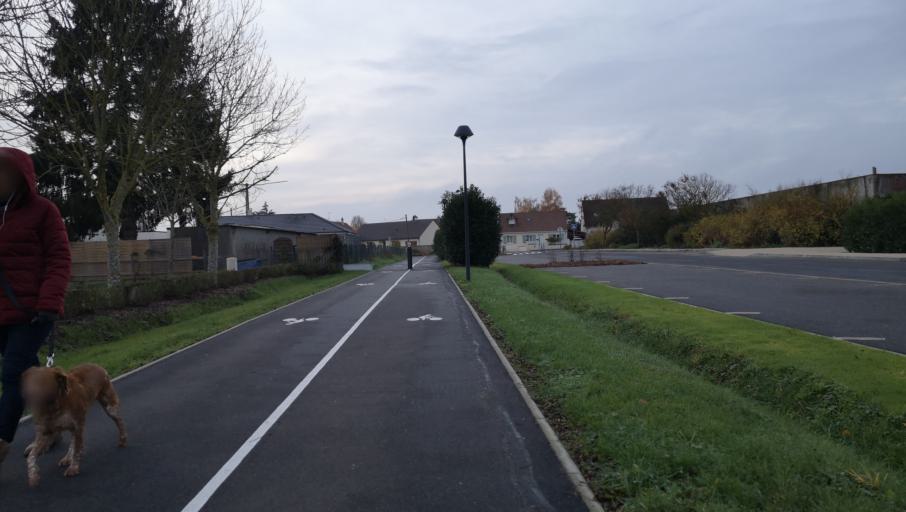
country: FR
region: Centre
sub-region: Departement du Loiret
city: Semoy
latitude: 47.9371
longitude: 1.9488
